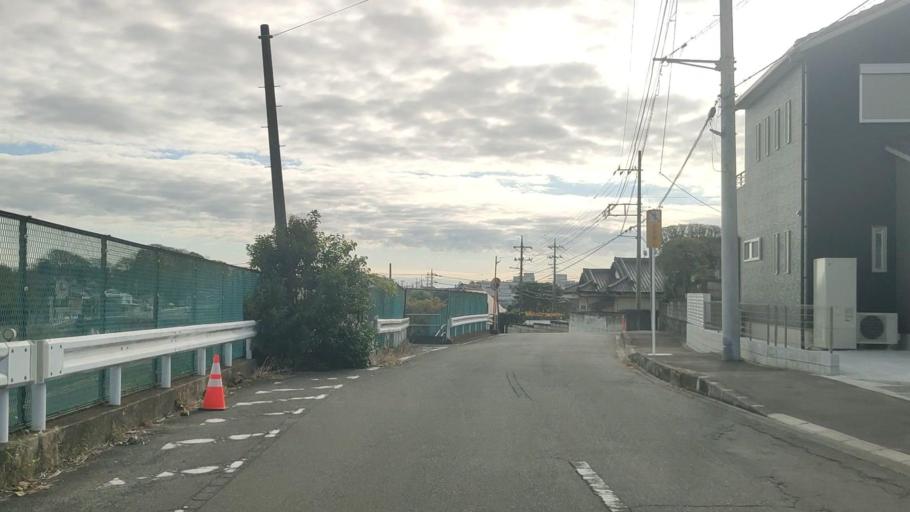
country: JP
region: Kanagawa
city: Minami-rinkan
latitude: 35.4850
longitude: 139.4692
